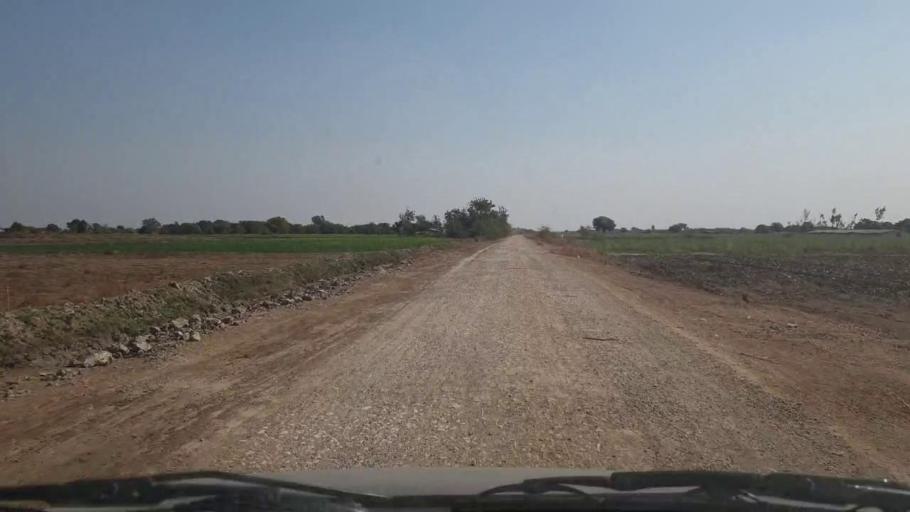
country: PK
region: Sindh
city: Samaro
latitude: 25.2224
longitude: 69.3328
